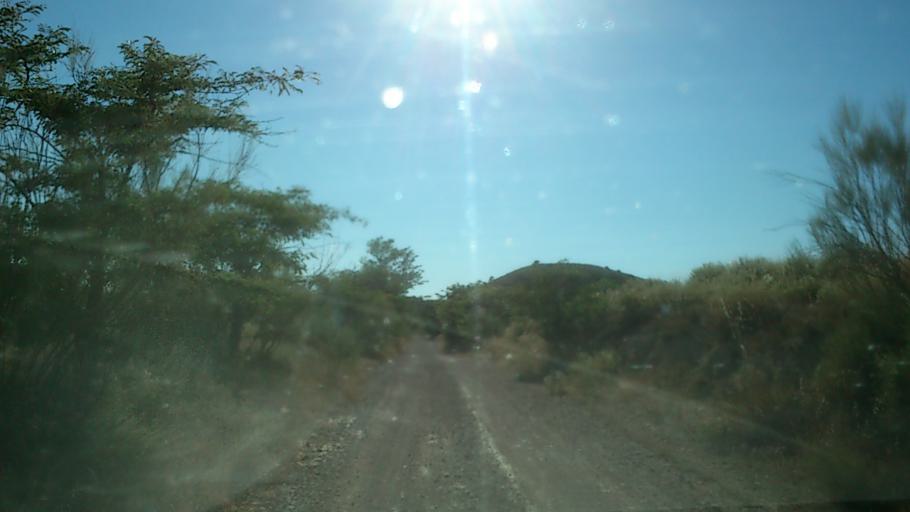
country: ES
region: Aragon
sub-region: Provincia de Zaragoza
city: San Mateo de Gallego
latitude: 41.7680
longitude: -0.7487
